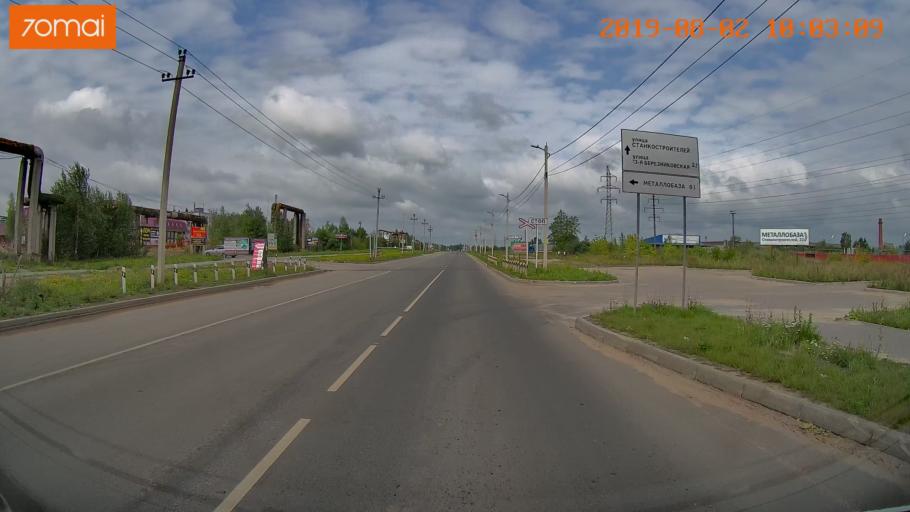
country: RU
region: Ivanovo
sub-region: Gorod Ivanovo
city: Ivanovo
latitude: 56.9661
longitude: 40.9471
